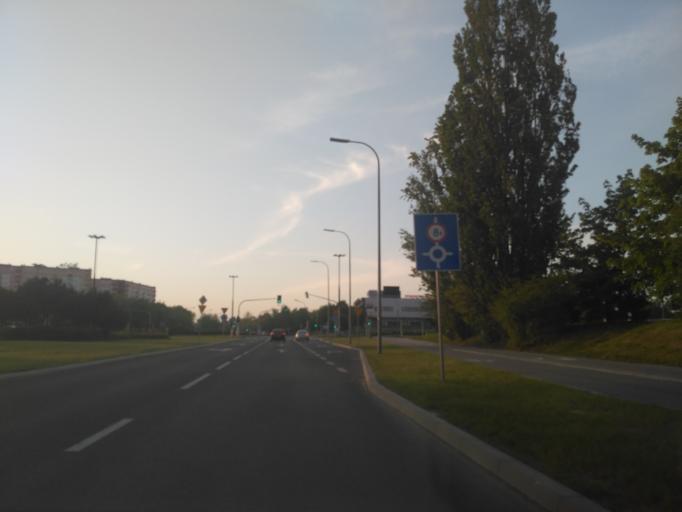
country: PL
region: Lublin Voivodeship
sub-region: Powiat lubelski
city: Lublin
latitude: 51.2614
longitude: 22.5525
